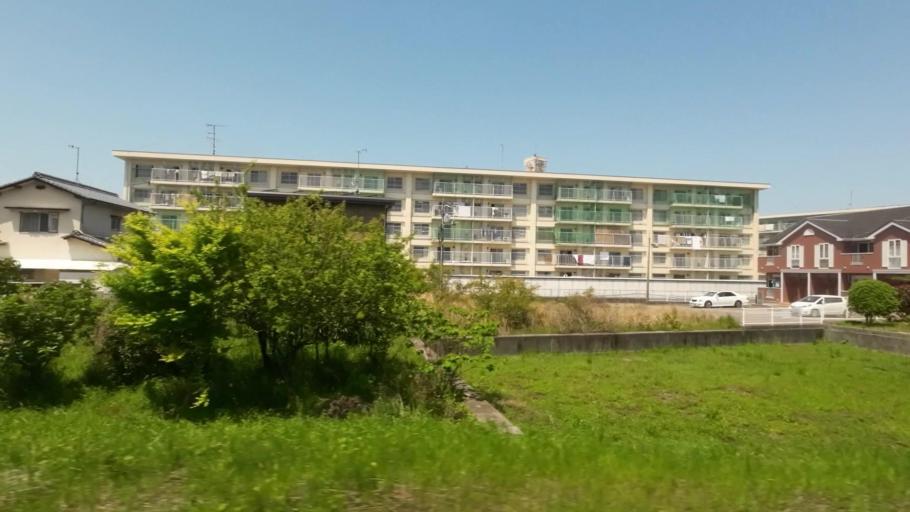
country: JP
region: Ehime
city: Hojo
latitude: 33.9446
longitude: 132.7713
